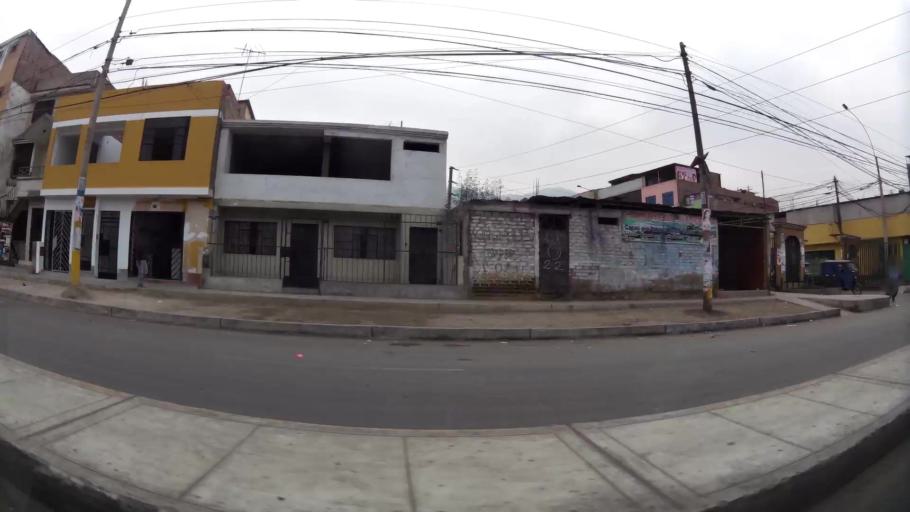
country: PE
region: Lima
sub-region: Lima
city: Independencia
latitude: -11.9833
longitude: -77.0139
